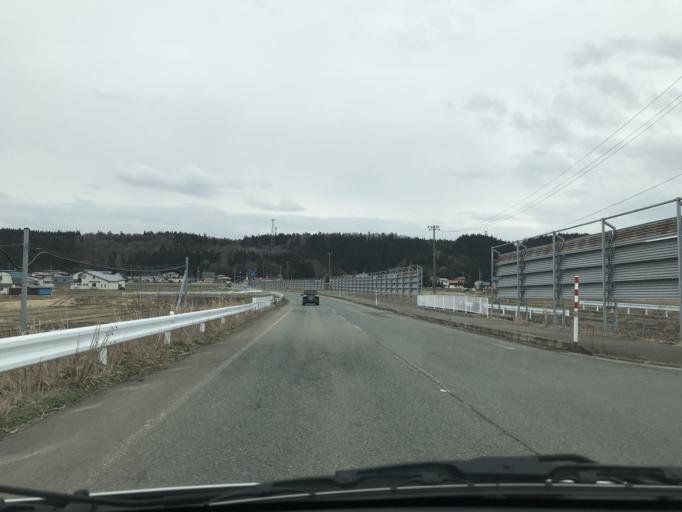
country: JP
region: Iwate
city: Kitakami
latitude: 39.2868
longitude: 141.0324
